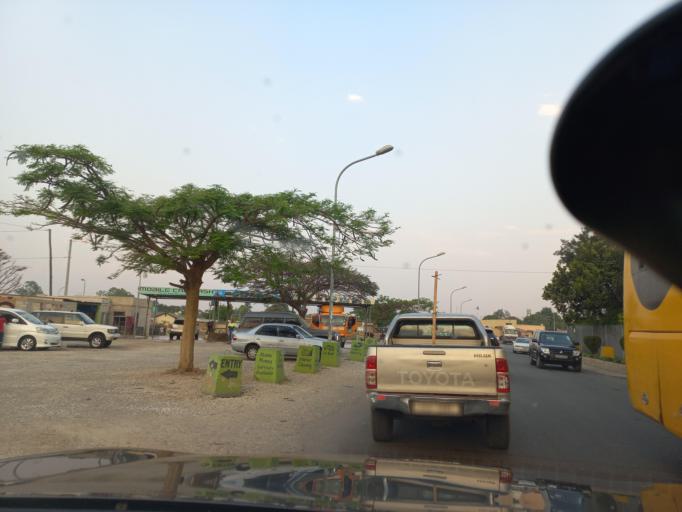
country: ZM
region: Lusaka
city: Lusaka
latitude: -15.4046
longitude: 28.2808
